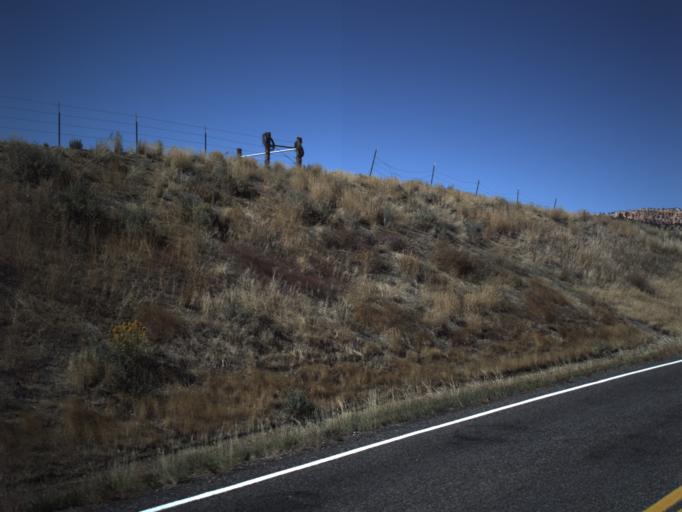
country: US
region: Utah
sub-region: Garfield County
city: Panguitch
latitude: 37.6418
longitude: -112.0814
